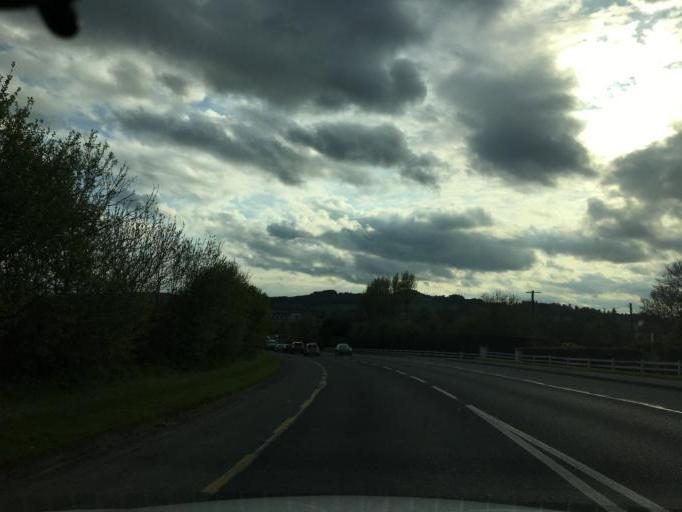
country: IE
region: Leinster
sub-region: Loch Garman
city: Loch Garman
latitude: 52.3403
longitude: -6.5082
